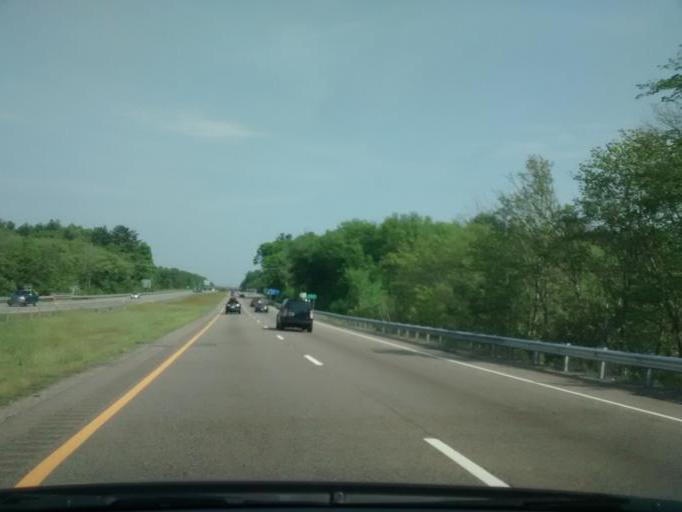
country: US
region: Massachusetts
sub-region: Plymouth County
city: Middleborough Center
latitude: 41.8789
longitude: -70.9128
